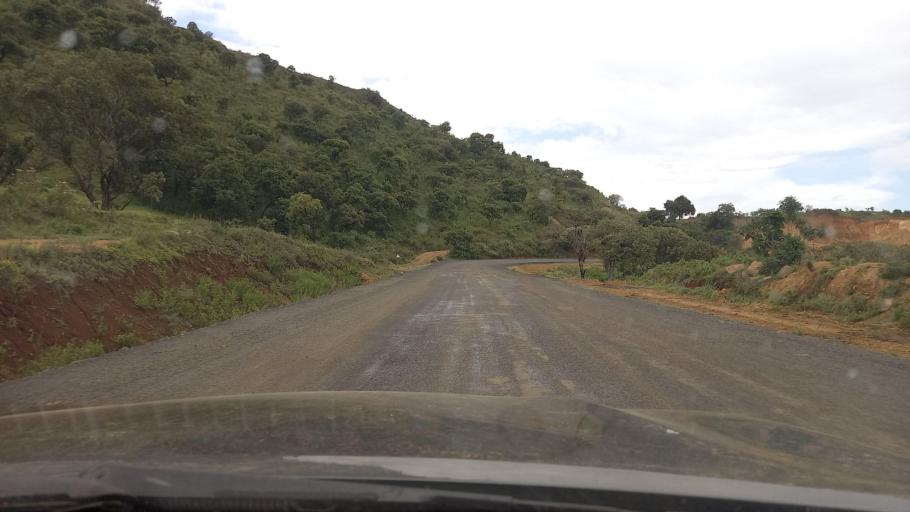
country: ET
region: Southern Nations, Nationalities, and People's Region
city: Mizan Teferi
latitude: 6.2057
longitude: 35.6534
